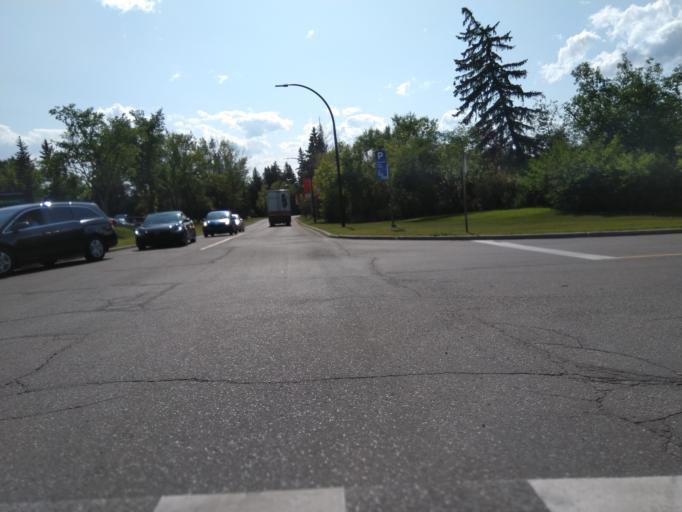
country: CA
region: Alberta
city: Calgary
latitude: 51.0760
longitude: -114.1253
